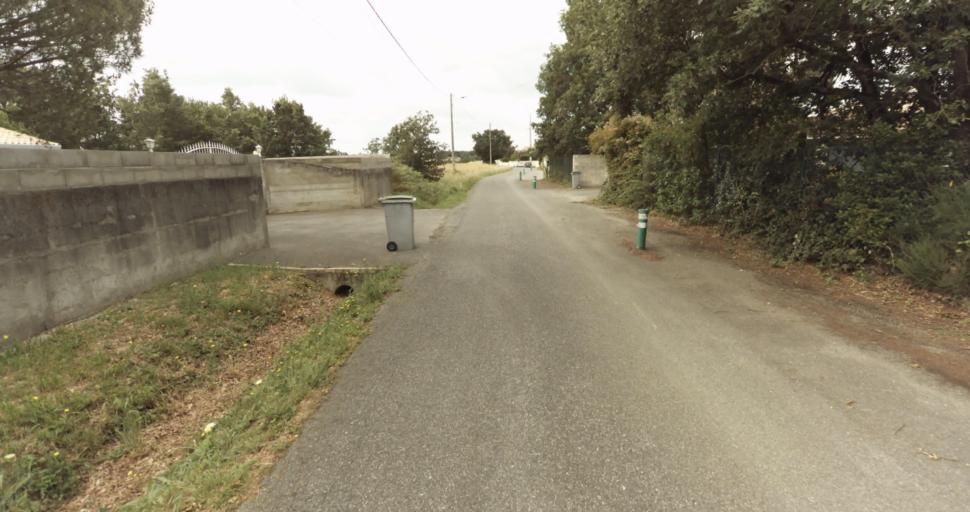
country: FR
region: Midi-Pyrenees
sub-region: Departement de la Haute-Garonne
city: Fonsorbes
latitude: 43.5493
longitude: 1.2182
